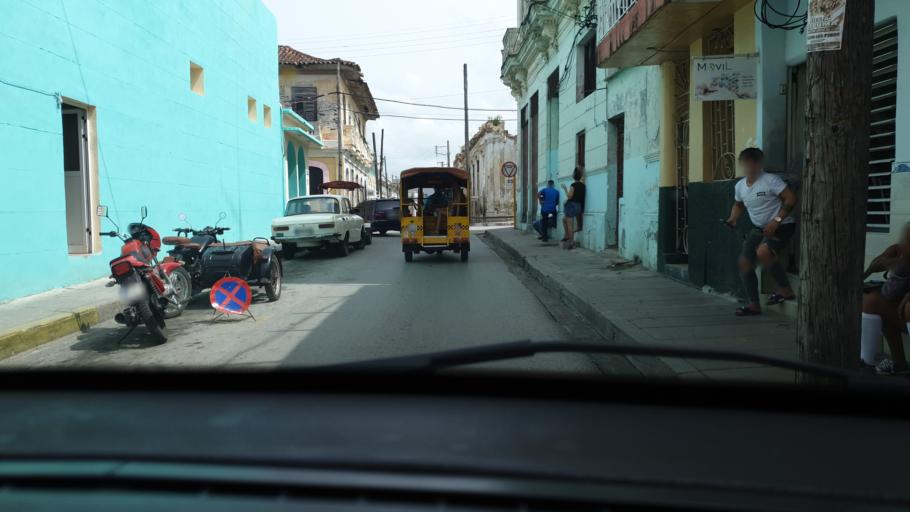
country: CU
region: Villa Clara
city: Santa Clara
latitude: 22.4065
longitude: -79.9669
